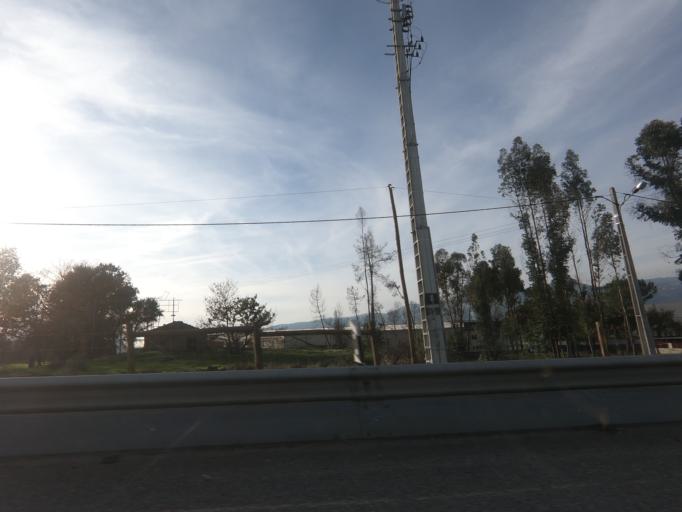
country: PT
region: Viseu
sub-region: Concelho de Tondela
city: Tondela
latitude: 40.5177
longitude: -8.0939
